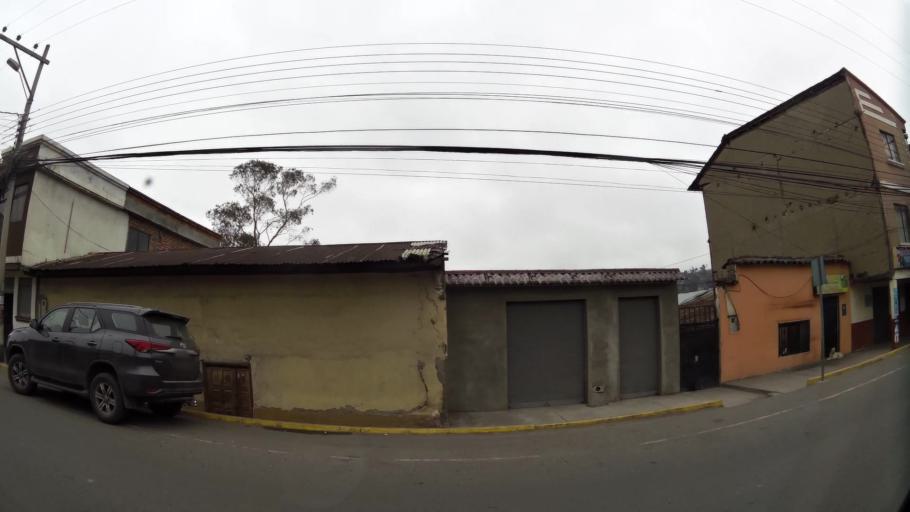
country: EC
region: Canar
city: Canar
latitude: -2.5109
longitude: -78.9288
